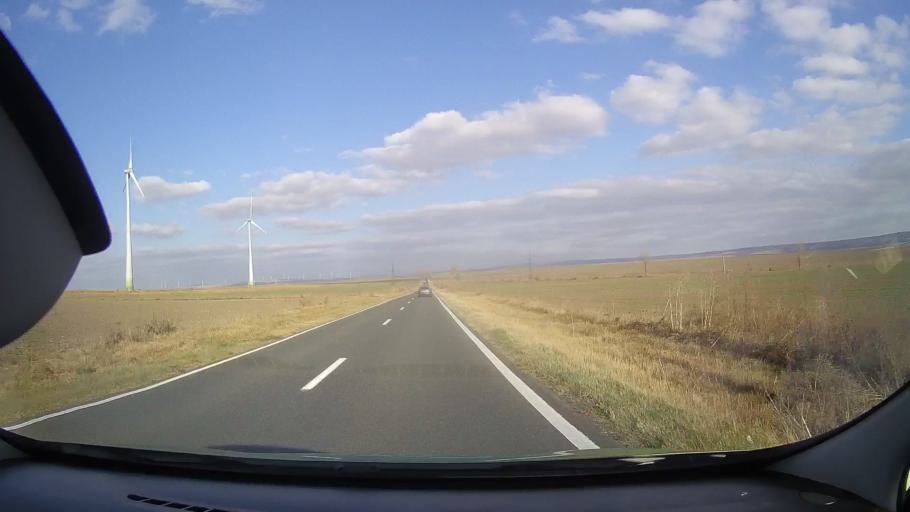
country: RO
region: Tulcea
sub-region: Comuna Topolog
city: Topolog
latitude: 44.8227
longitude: 28.2679
